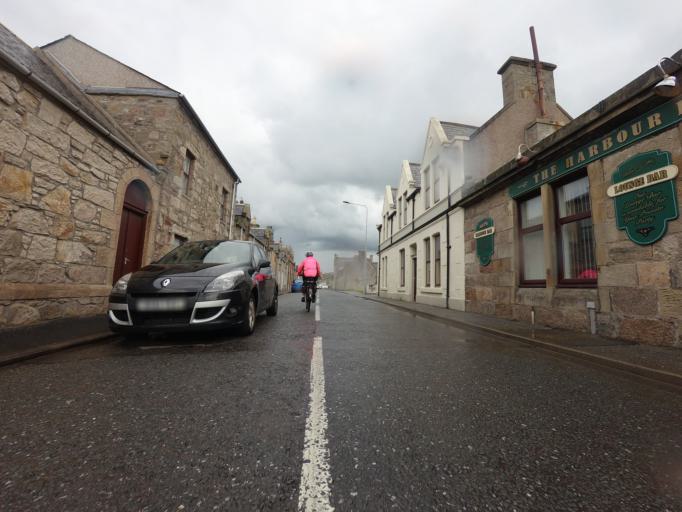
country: GB
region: Scotland
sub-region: Moray
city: Buckie
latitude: 57.6757
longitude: -2.9798
